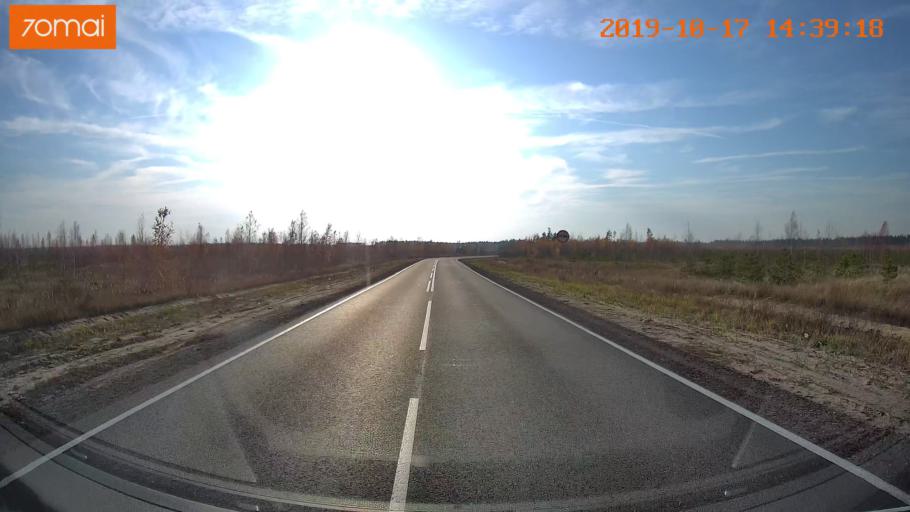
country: RU
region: Rjazan
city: Solotcha
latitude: 54.8629
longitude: 39.9736
